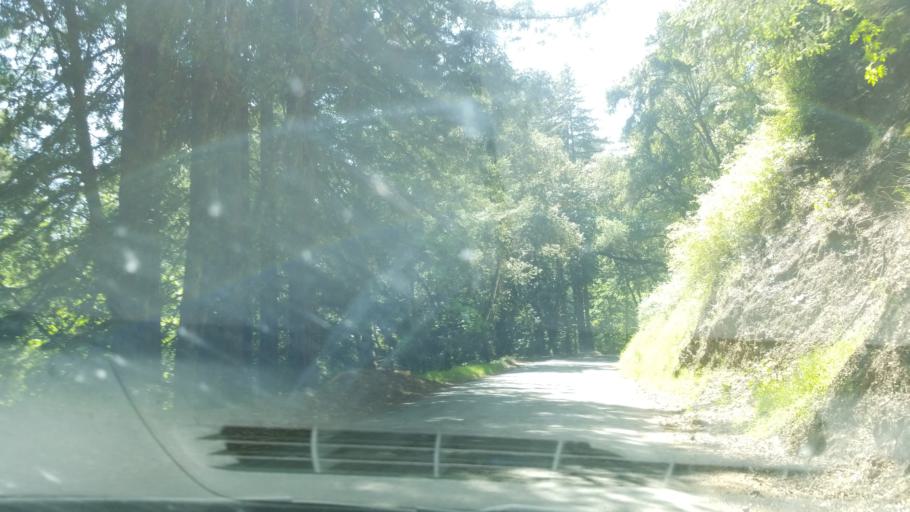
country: US
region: California
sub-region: Santa Cruz County
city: Day Valley
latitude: 37.0581
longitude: -121.8187
